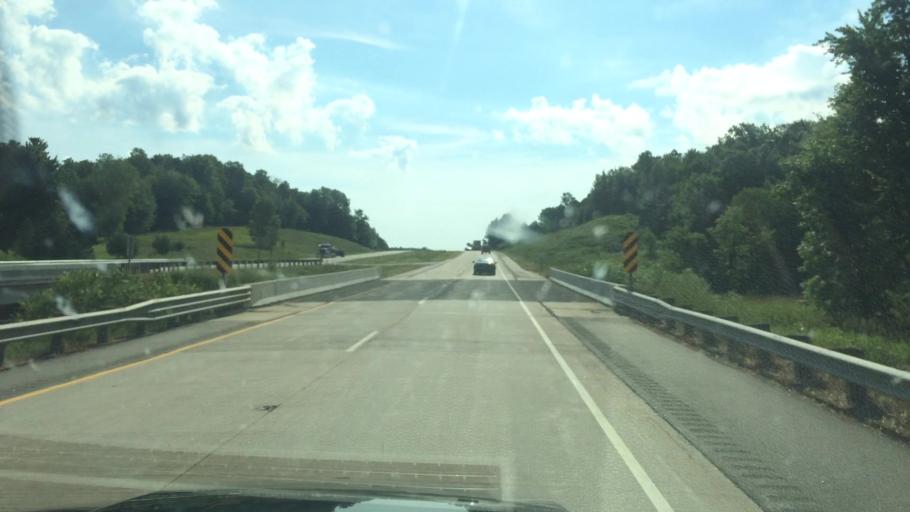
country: US
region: Wisconsin
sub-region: Shawano County
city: Wittenberg
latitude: 44.8036
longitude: -89.0172
